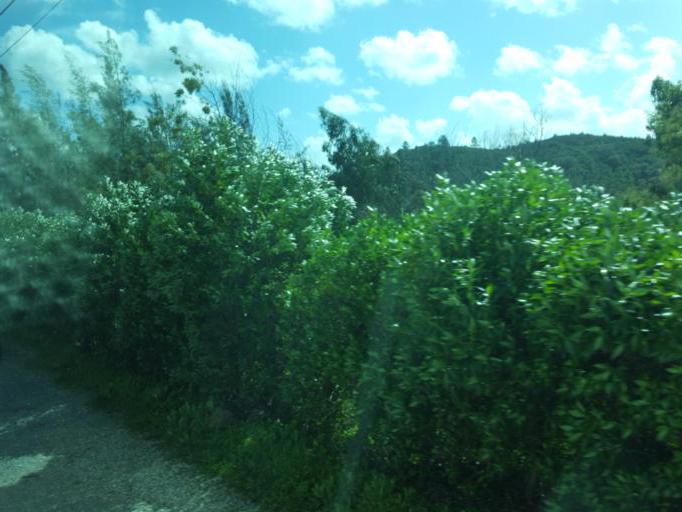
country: PT
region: Faro
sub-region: Monchique
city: Monchique
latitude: 37.2796
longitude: -8.5543
